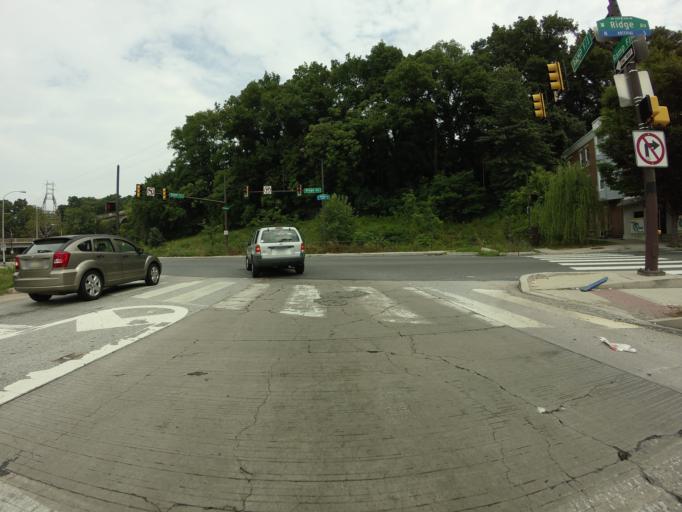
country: US
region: Pennsylvania
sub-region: Montgomery County
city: Bala-Cynwyd
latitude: 40.0142
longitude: -75.2049
